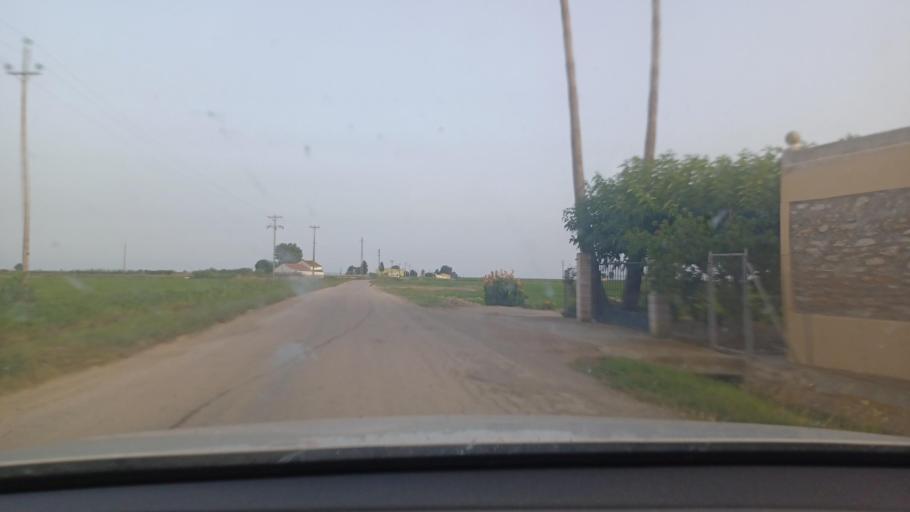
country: ES
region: Catalonia
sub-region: Provincia de Tarragona
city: Deltebre
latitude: 40.6782
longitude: 0.6592
